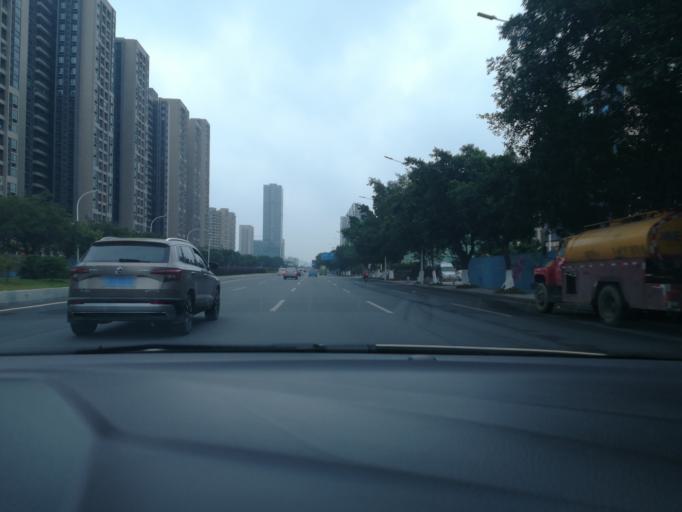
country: CN
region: Guangdong
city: Nansha
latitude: 22.8007
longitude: 113.5666
